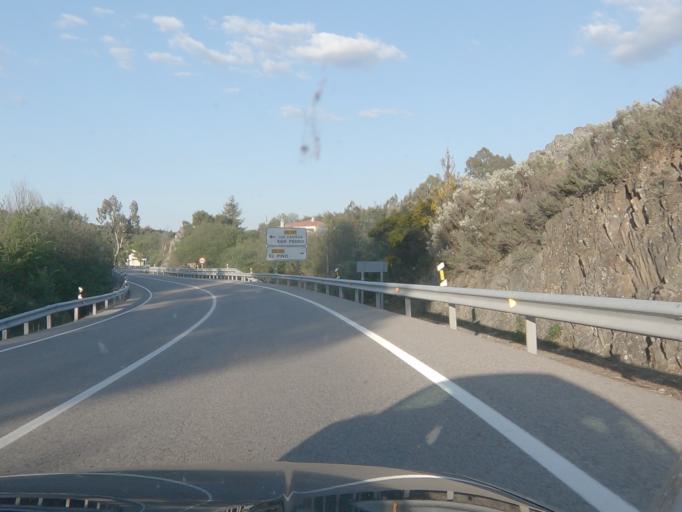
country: PT
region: Portalegre
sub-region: Portalegre
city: Sao Juliao
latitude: 39.3417
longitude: -7.2885
